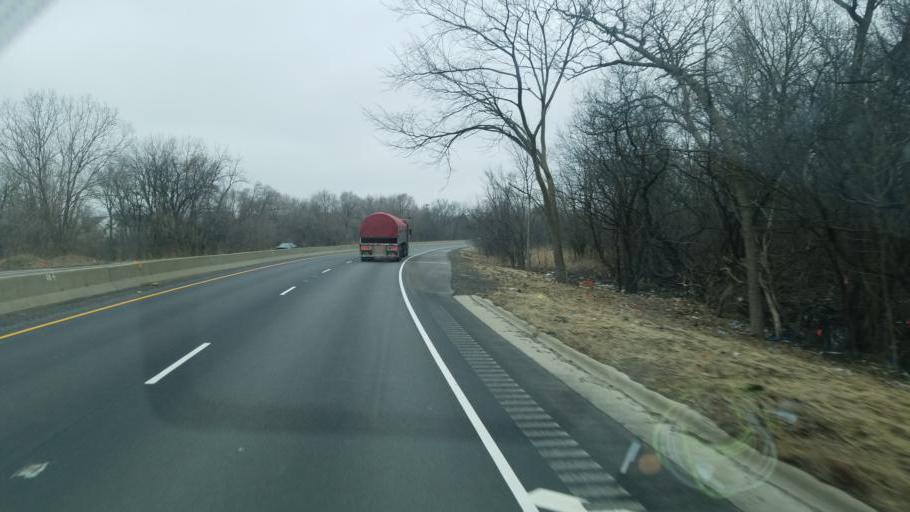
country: US
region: Illinois
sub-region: Lake County
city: Knollwood
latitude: 42.2896
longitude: -87.8747
